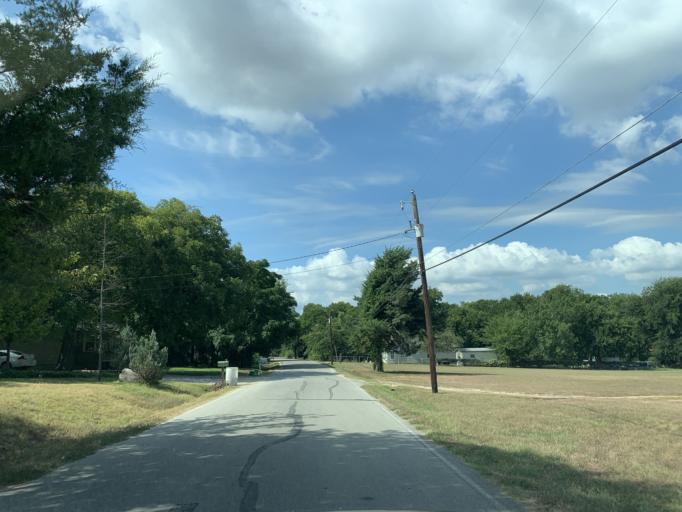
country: US
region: Texas
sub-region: Tarrant County
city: Azle
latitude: 32.8668
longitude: -97.5277
